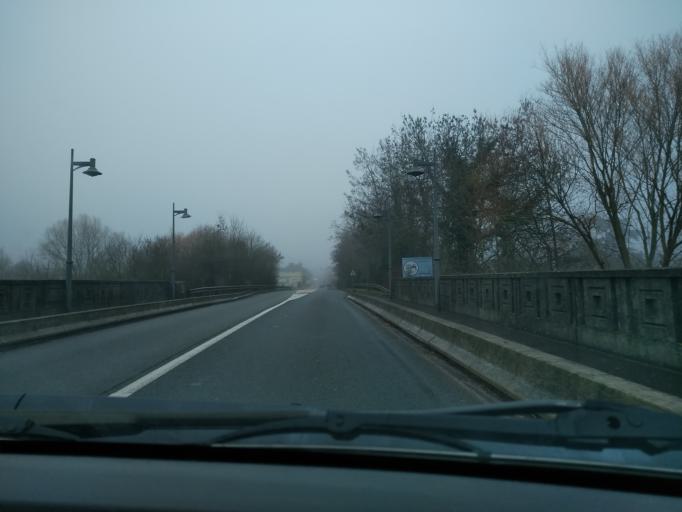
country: FR
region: Centre
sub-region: Departement d'Eure-et-Loir
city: Marboue
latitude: 48.1109
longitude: 1.3301
